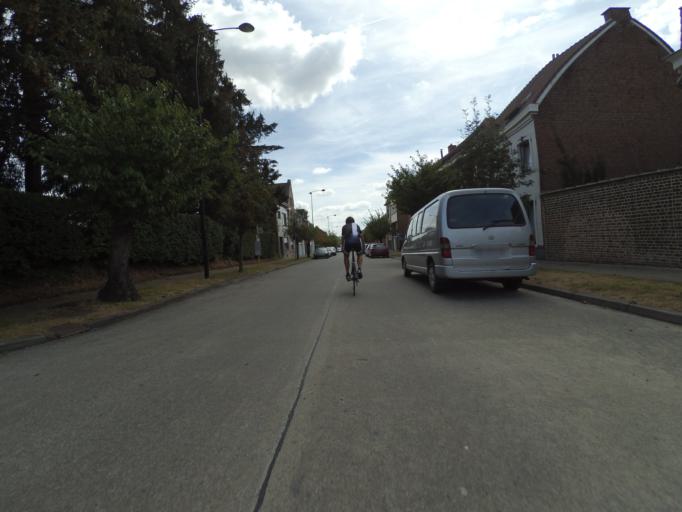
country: BE
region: Flanders
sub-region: Provincie Oost-Vlaanderen
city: Ronse
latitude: 50.7393
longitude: 3.5984
